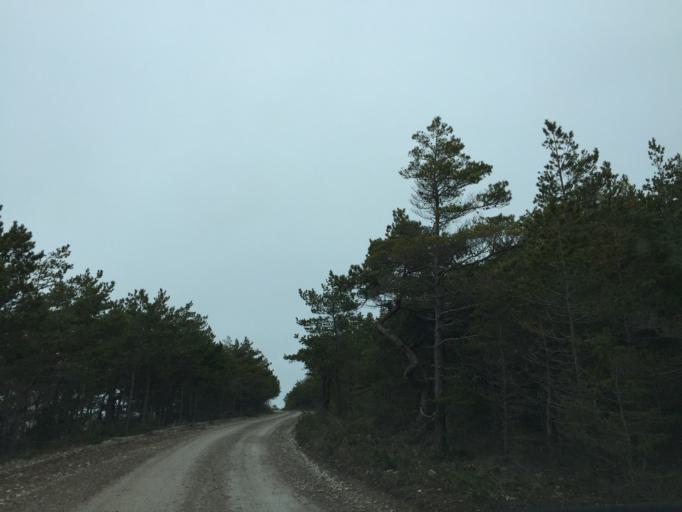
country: EE
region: Saare
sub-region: Kuressaare linn
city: Kuressaare
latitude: 58.5053
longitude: 21.9116
